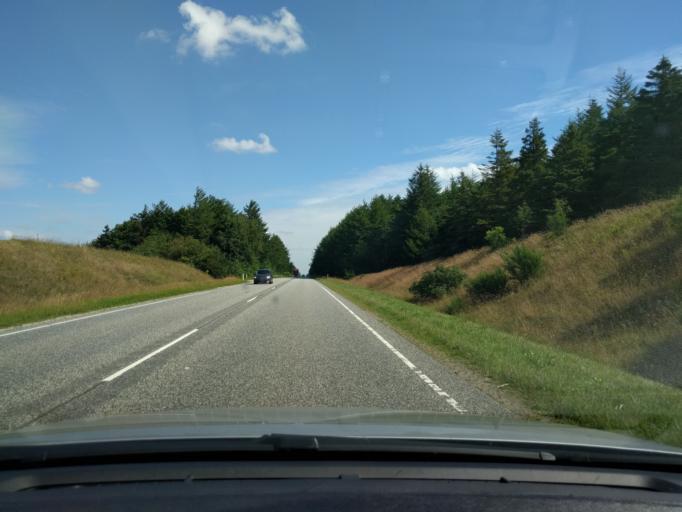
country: DK
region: Central Jutland
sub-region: Herning Kommune
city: Kibaek
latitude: 56.0537
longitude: 8.8877
